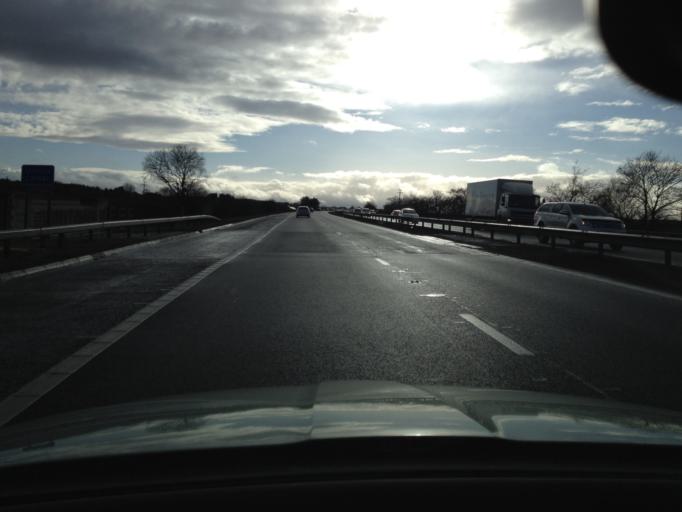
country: GB
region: Scotland
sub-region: West Lothian
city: Broxburn
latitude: 55.9243
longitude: -3.4570
